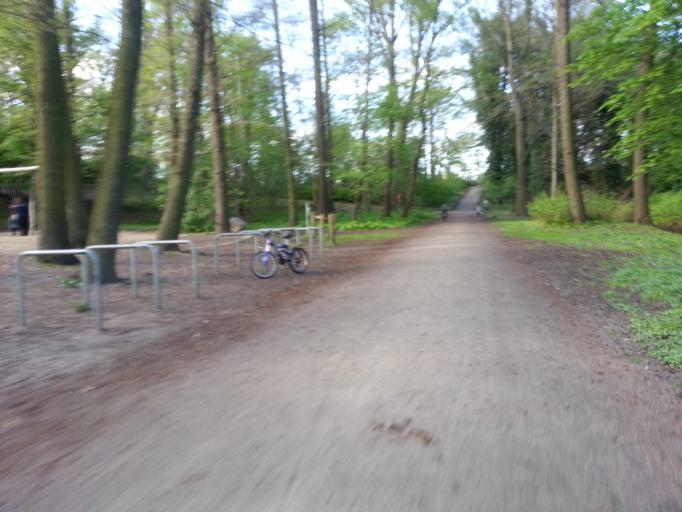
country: DE
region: Berlin
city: Charlottenburg-Nord
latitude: 52.5281
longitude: 13.2935
